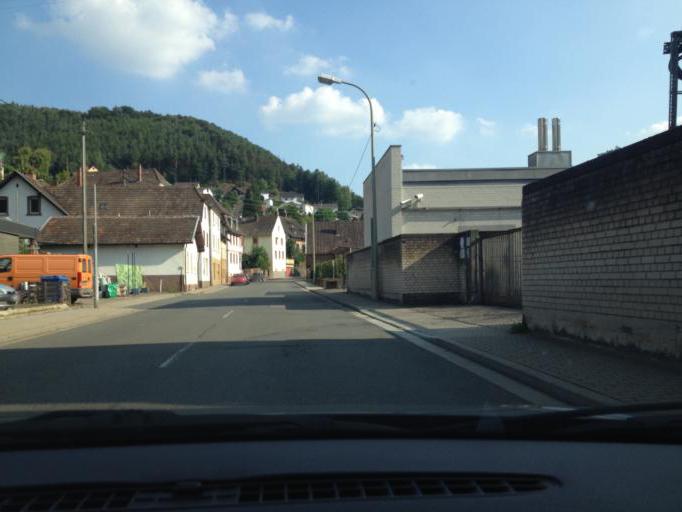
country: DE
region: Rheinland-Pfalz
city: Neidenfels
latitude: 49.3884
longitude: 8.0453
